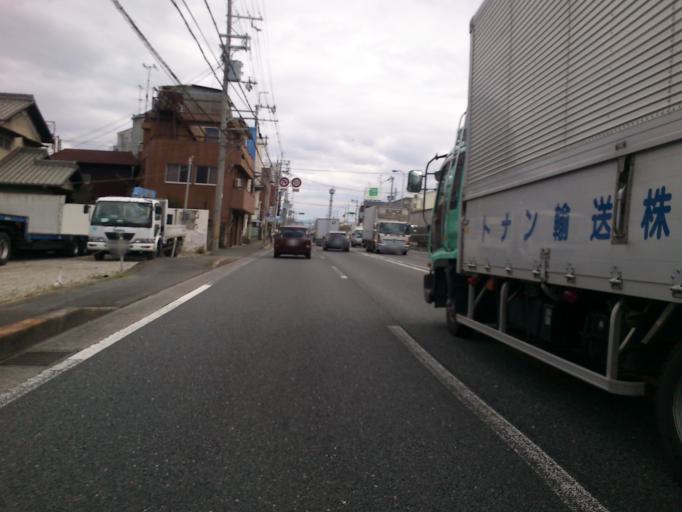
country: JP
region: Kyoto
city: Yawata
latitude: 34.8823
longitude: 135.6735
